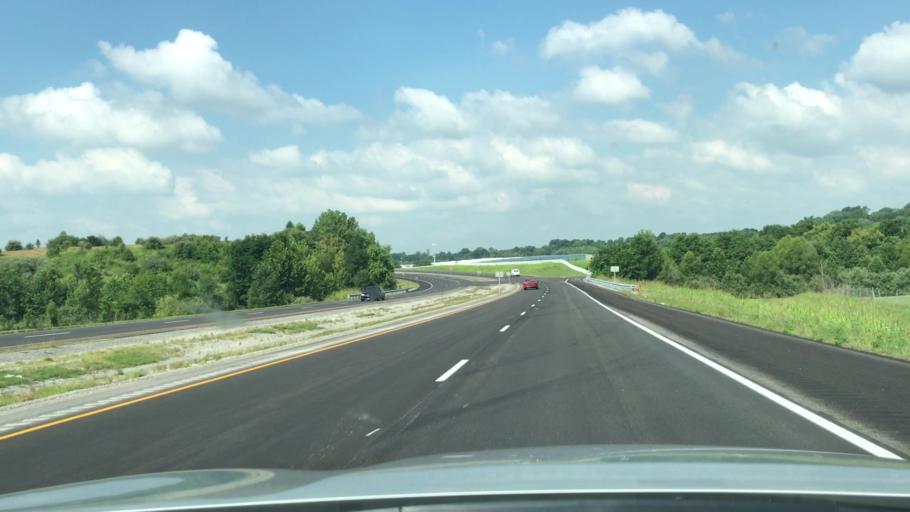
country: US
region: Kentucky
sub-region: Barren County
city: Glasgow
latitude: 37.0278
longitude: -85.9279
